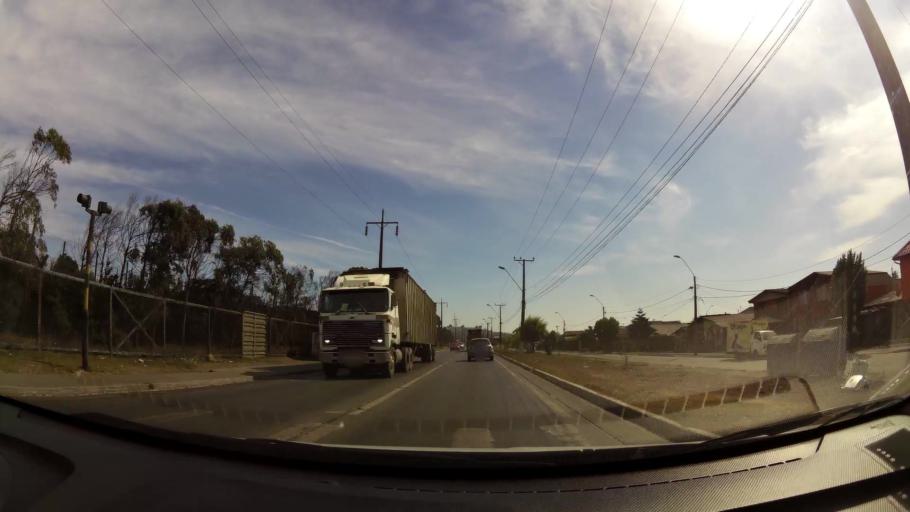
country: CL
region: Biobio
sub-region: Provincia de Concepcion
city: Talcahuano
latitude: -36.7340
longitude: -73.1194
